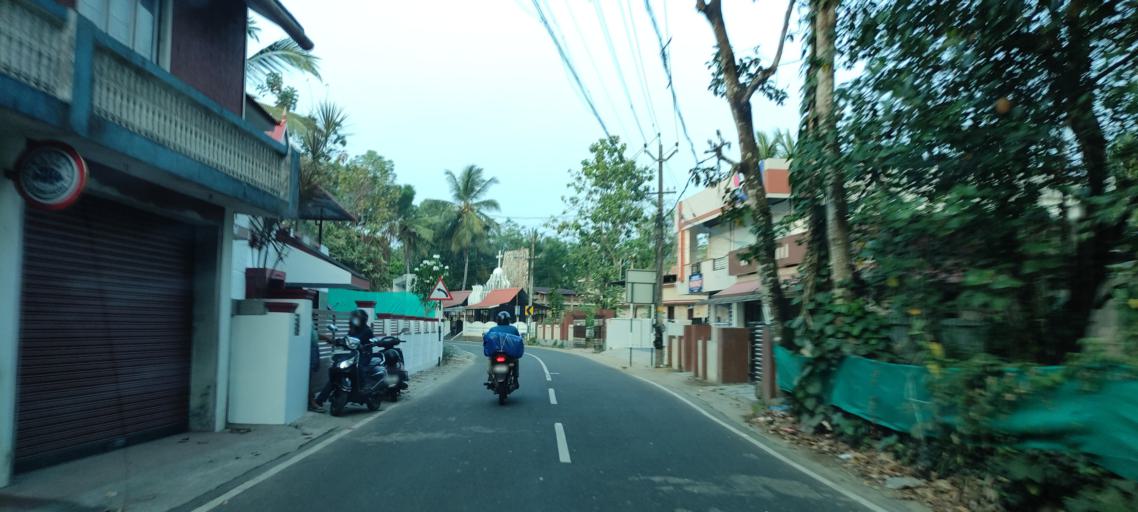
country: IN
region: Kerala
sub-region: Alappuzha
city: Mavelikara
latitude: 9.2629
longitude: 76.5560
